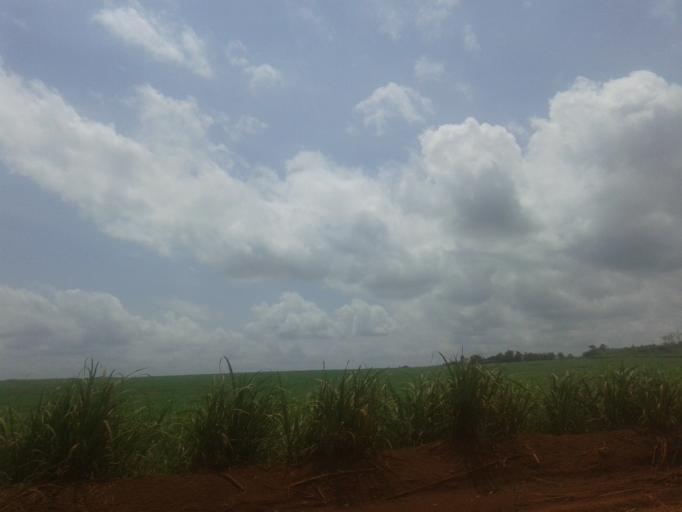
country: CM
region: Centre
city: Mbandjok
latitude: 4.4461
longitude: 11.9515
